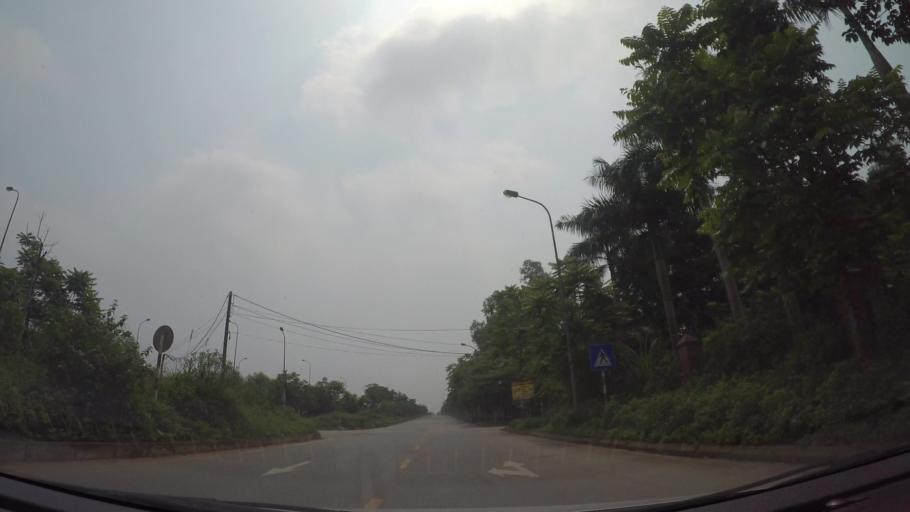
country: VN
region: Ha Noi
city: Lien Quan
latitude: 20.9893
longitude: 105.5593
